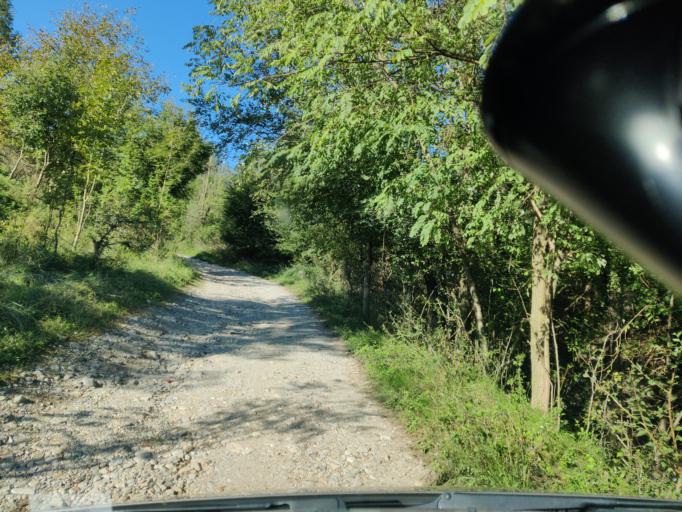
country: IT
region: Veneto
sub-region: Provincia di Belluno
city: Ponte nelle Alpi-Polpet
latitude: 46.1706
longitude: 12.2570
